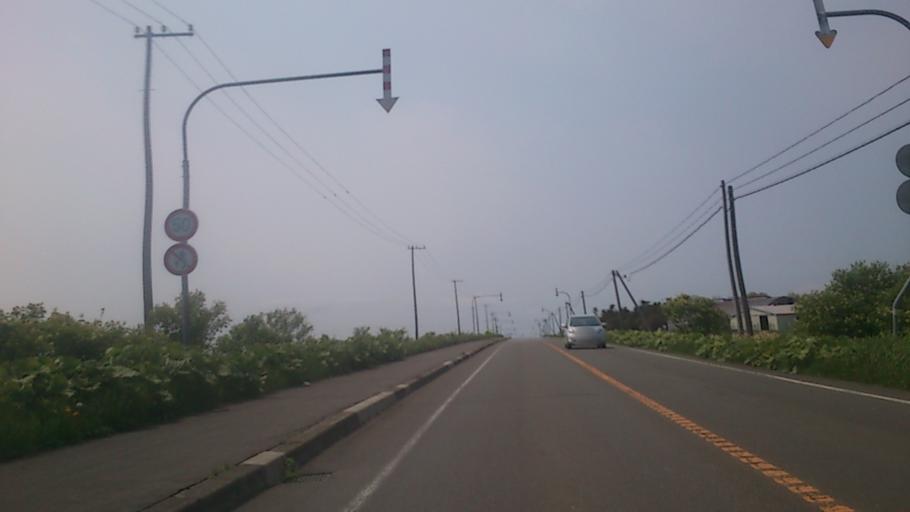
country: JP
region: Hokkaido
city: Nemuro
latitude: 43.2726
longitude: 145.5332
